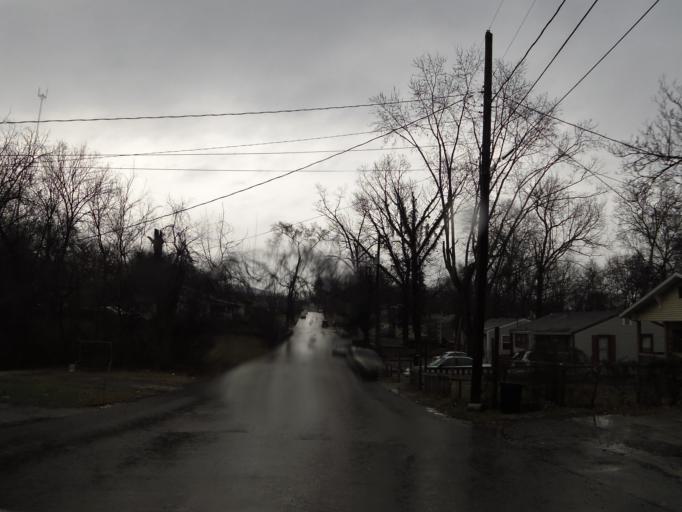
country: US
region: Tennessee
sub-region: Knox County
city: Knoxville
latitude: 35.9838
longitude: -83.9587
